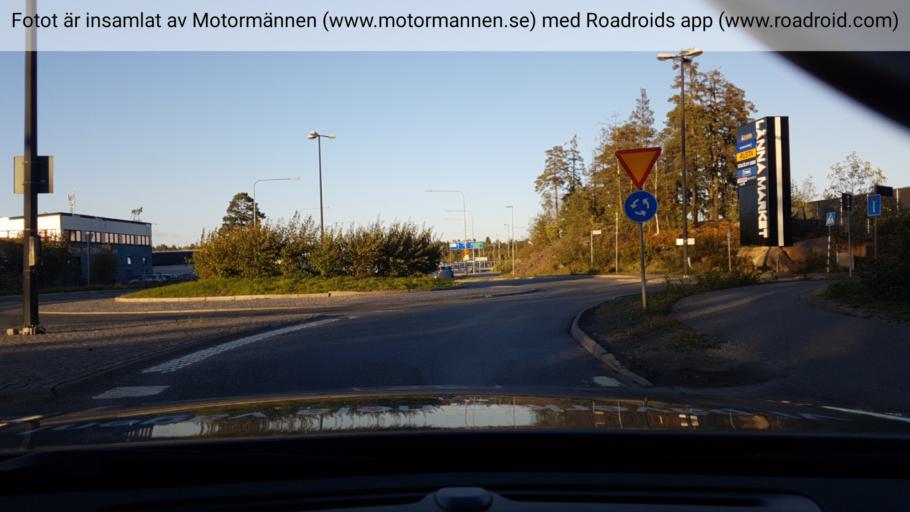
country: SE
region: Stockholm
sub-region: Haninge Kommun
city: Handen
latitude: 59.1985
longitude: 18.1241
